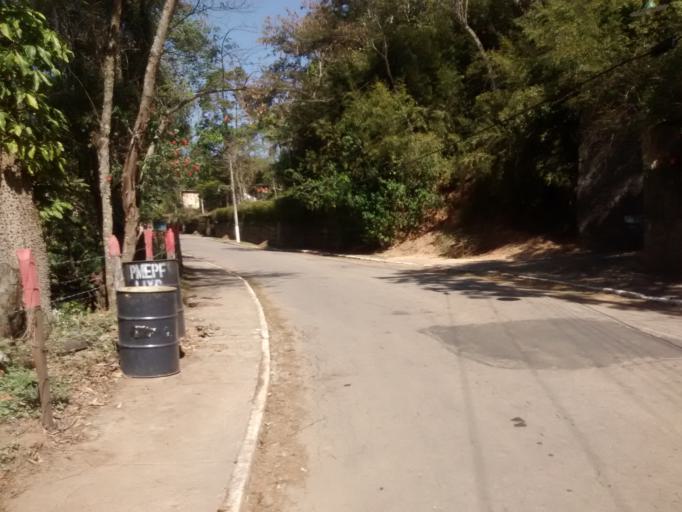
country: BR
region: Rio de Janeiro
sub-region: Vassouras
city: Vassouras
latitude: -22.4745
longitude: -43.5838
